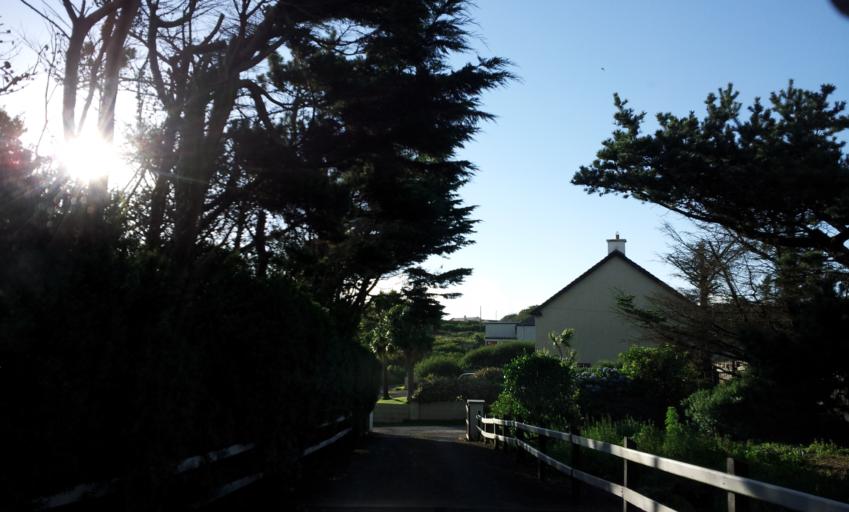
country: IE
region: Munster
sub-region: Ciarrai
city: Dingle
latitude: 52.1224
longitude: -10.3252
